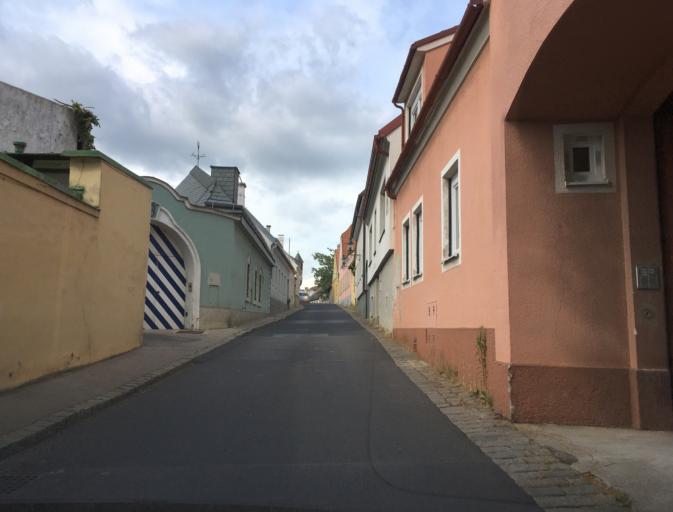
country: AT
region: Lower Austria
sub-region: Politischer Bezirk Modling
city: Gumpoldskirchen
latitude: 48.0459
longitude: 16.2771
